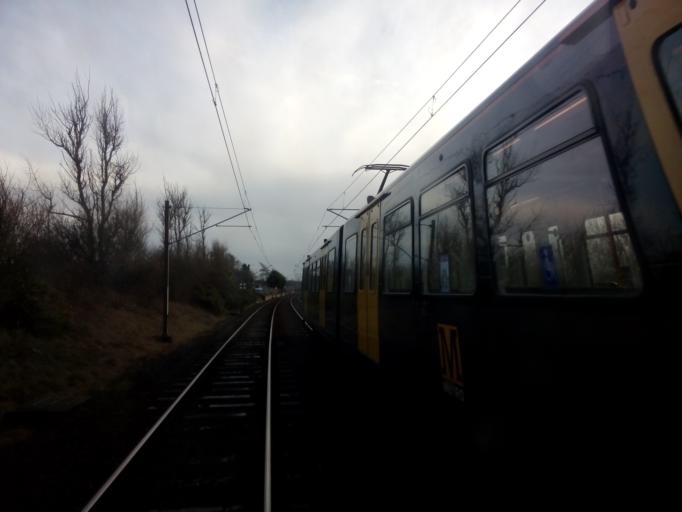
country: GB
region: England
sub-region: Newcastle upon Tyne
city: Dinnington
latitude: 55.0310
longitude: -1.7067
